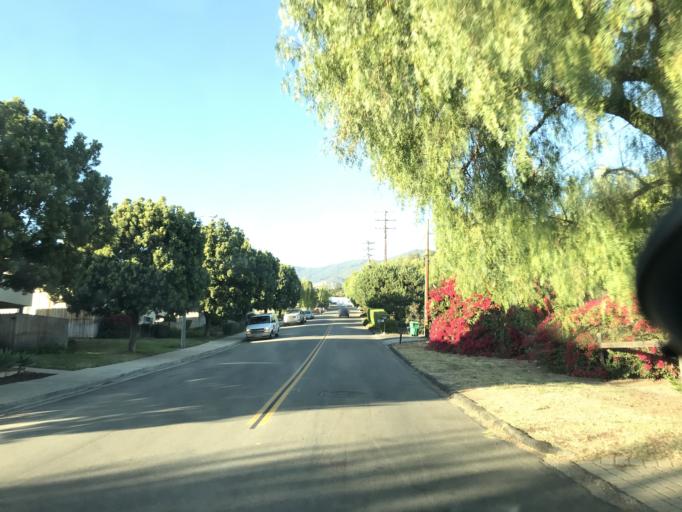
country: US
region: California
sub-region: Santa Barbara County
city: Mission Canyon
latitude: 34.4541
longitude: -119.7598
